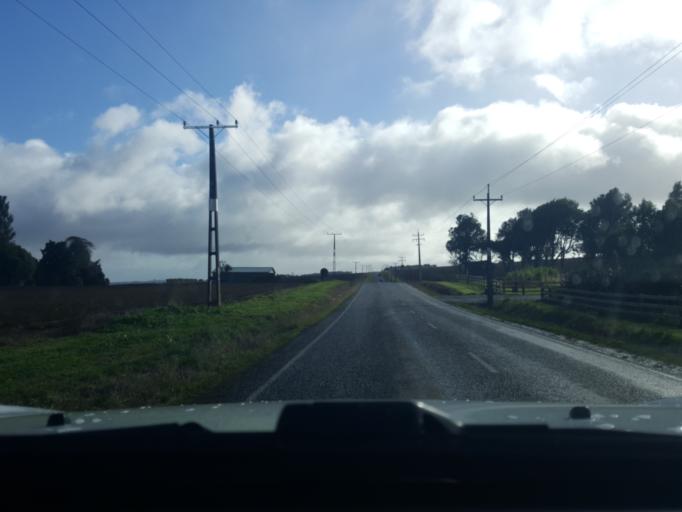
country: NZ
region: Auckland
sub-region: Auckland
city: Pukekohe East
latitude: -37.3254
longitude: 174.9863
